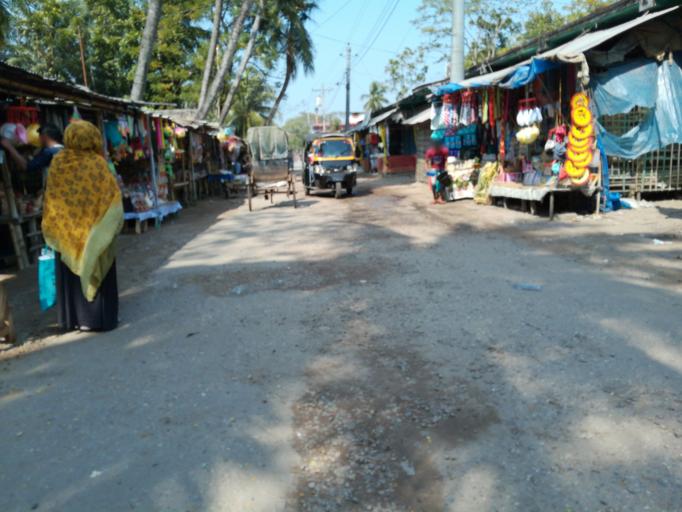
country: BD
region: Khulna
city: Morrelgonj
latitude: 22.6632
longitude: 89.7587
